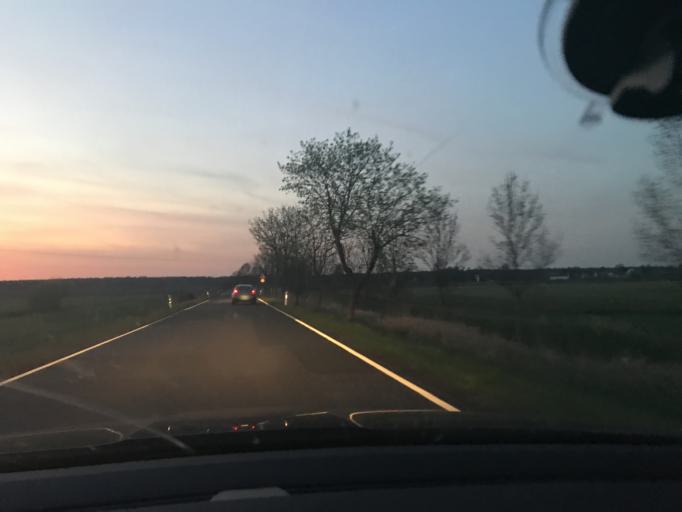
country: DE
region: Brandenburg
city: Grunewald
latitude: 51.3909
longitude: 13.9885
